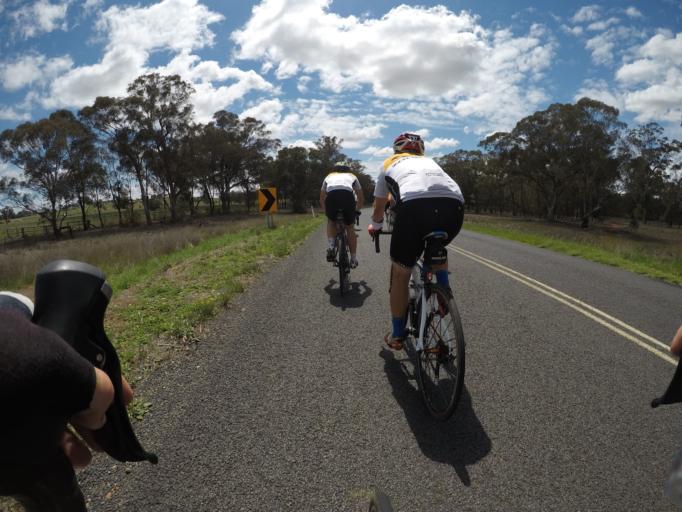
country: AU
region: New South Wales
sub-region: Dubbo Municipality
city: Dubbo
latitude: -32.3866
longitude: 148.5721
